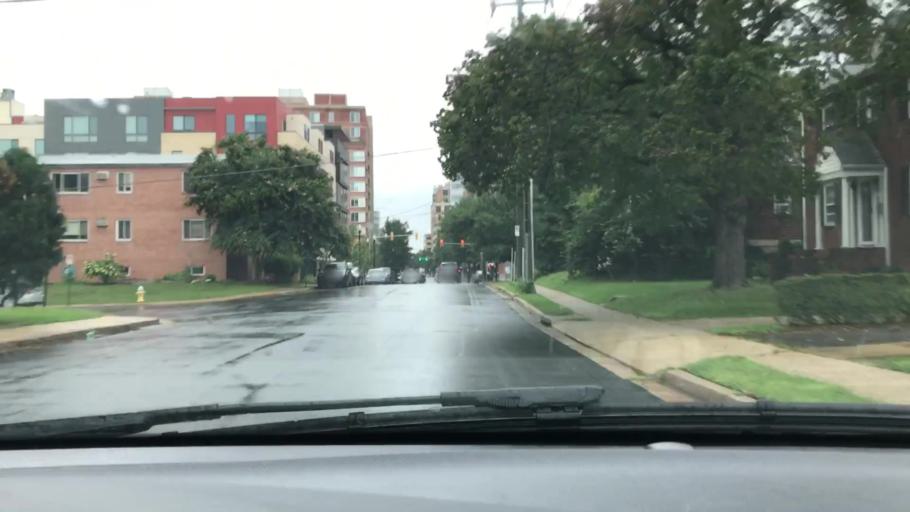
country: US
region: Virginia
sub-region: Arlington County
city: Arlington
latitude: 38.8833
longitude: -77.0945
